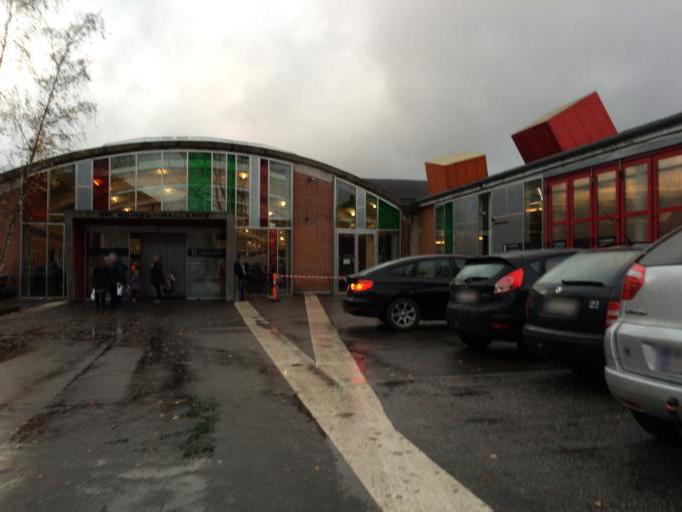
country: DK
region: South Denmark
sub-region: Vejle Kommune
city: Vejle
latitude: 55.7135
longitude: 9.5310
